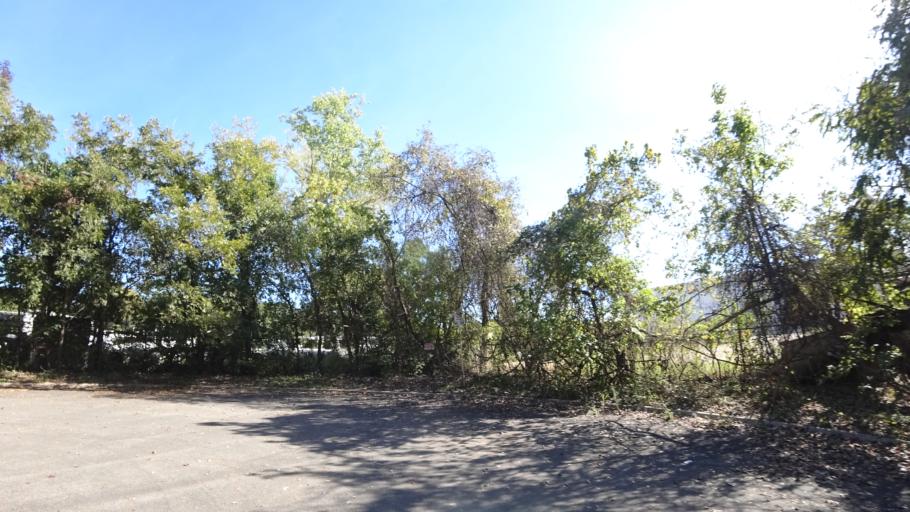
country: US
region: Texas
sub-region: Travis County
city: Austin
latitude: 30.2568
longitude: -97.6911
